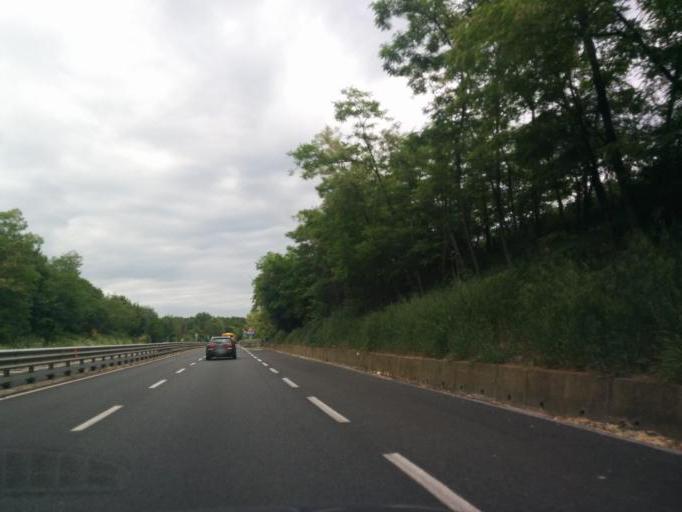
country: IT
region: Tuscany
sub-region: Provincia di Siena
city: Staggia
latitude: 43.4082
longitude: 11.1748
